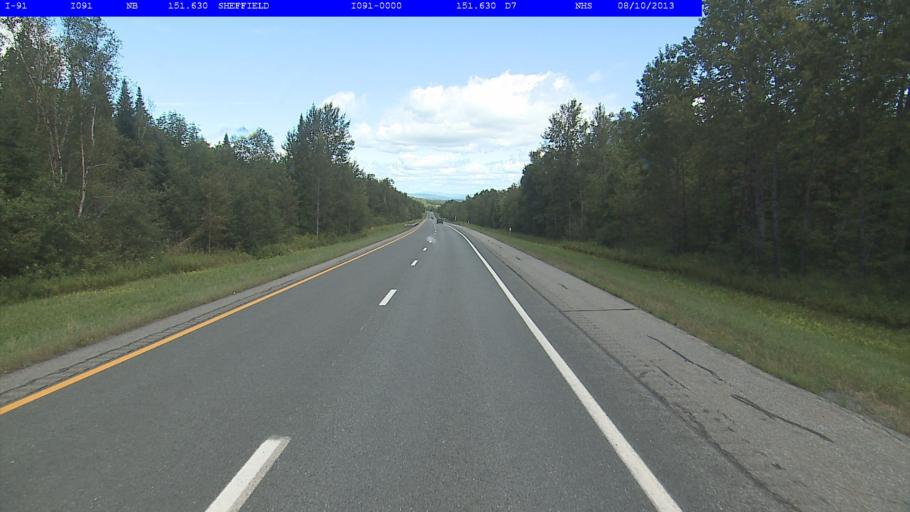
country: US
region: Vermont
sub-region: Caledonia County
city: Lyndonville
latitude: 44.6877
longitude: -72.1354
